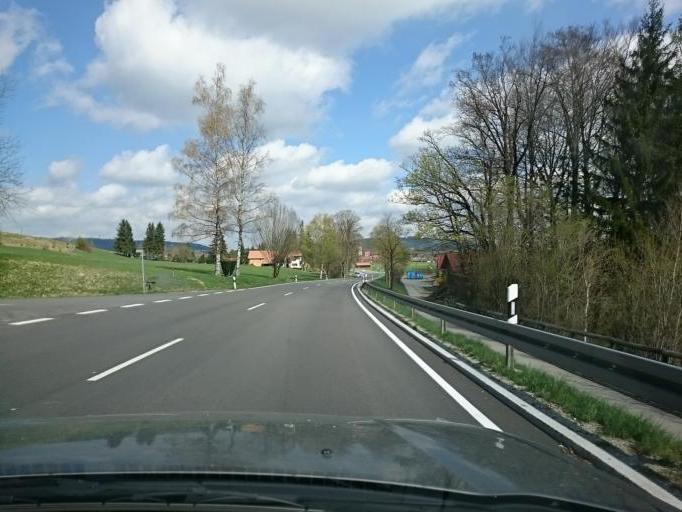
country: DE
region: Bavaria
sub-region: Upper Bavaria
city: Rottenbuch
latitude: 47.7238
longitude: 10.9685
